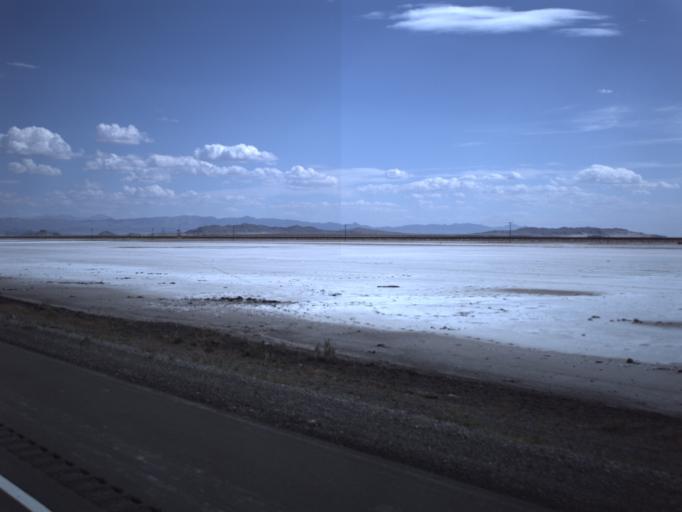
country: US
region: Utah
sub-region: Tooele County
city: Wendover
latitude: 40.7285
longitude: -113.3989
